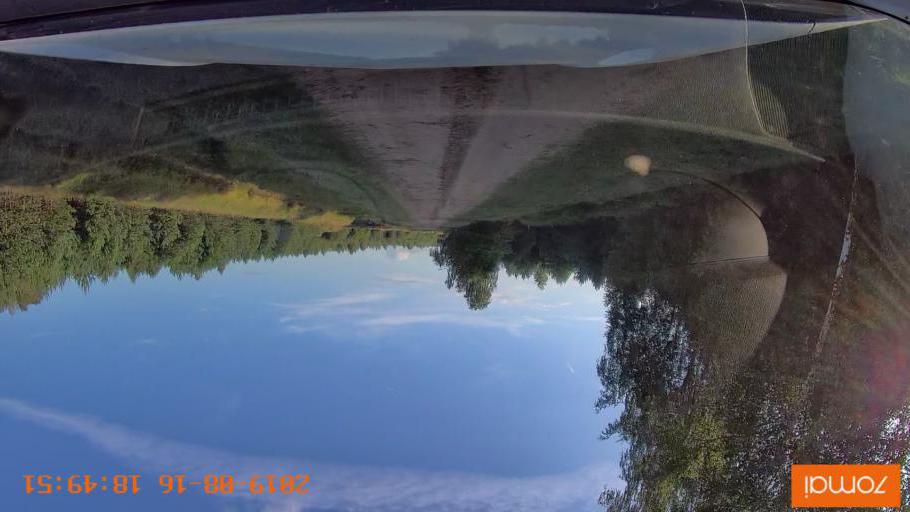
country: BY
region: Mogilev
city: Asipovichy
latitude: 53.2391
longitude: 28.6648
